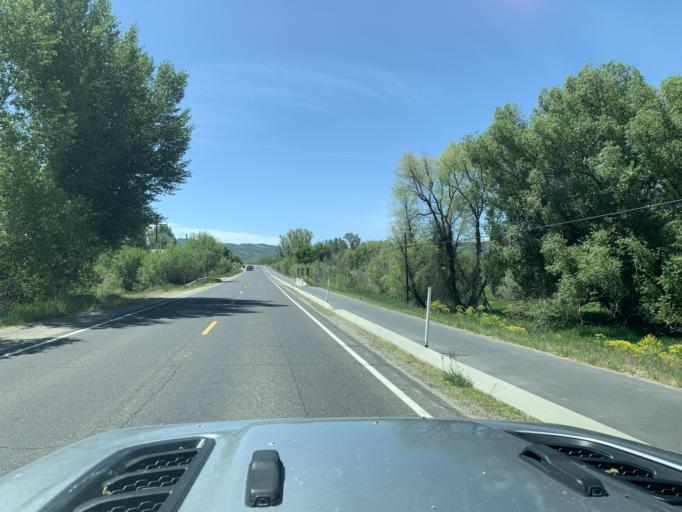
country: US
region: Utah
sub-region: Weber County
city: Wolf Creek
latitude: 41.2805
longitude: -111.7771
